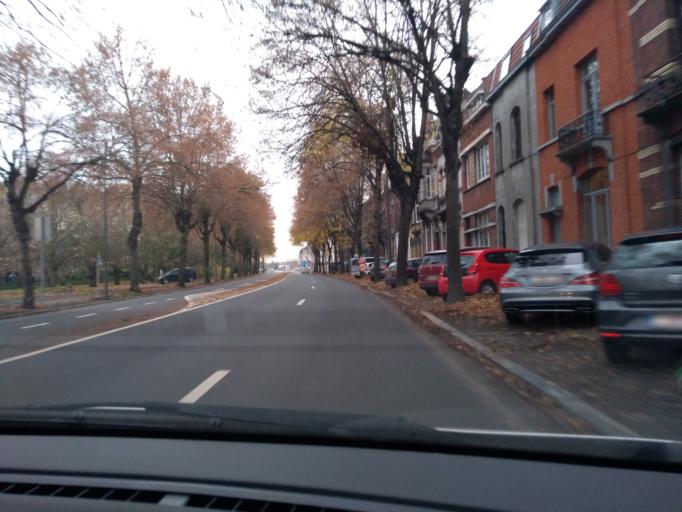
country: BE
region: Wallonia
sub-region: Province du Hainaut
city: Tournai
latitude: 50.6079
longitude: 3.4033
